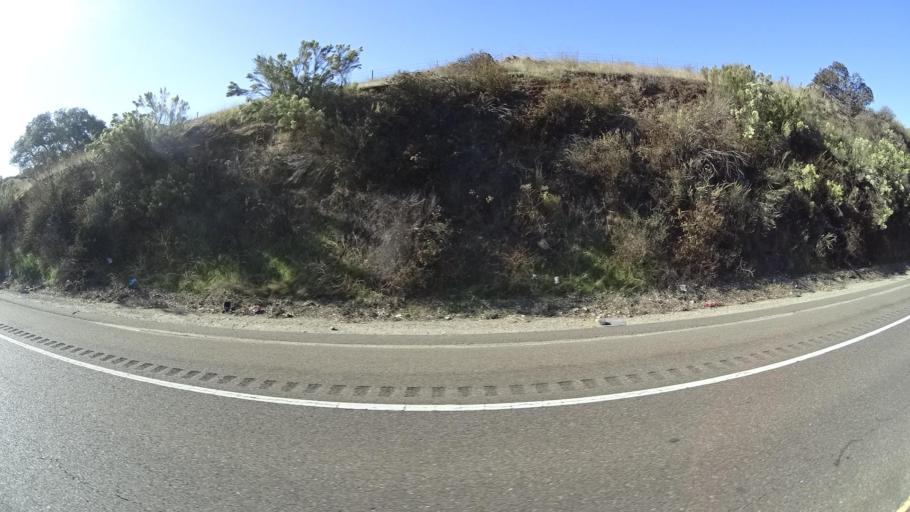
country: US
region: California
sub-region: San Diego County
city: Jamul
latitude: 32.6640
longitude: -116.8149
